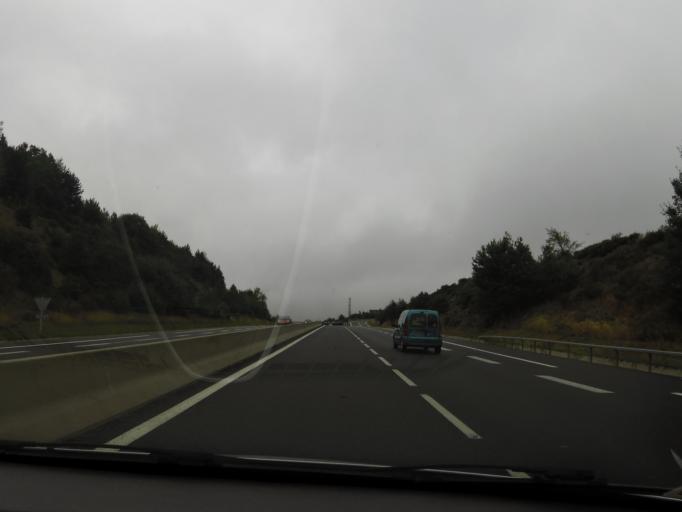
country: FR
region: Languedoc-Roussillon
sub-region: Departement de la Lozere
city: Marvejols
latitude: 44.5875
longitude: 3.2512
